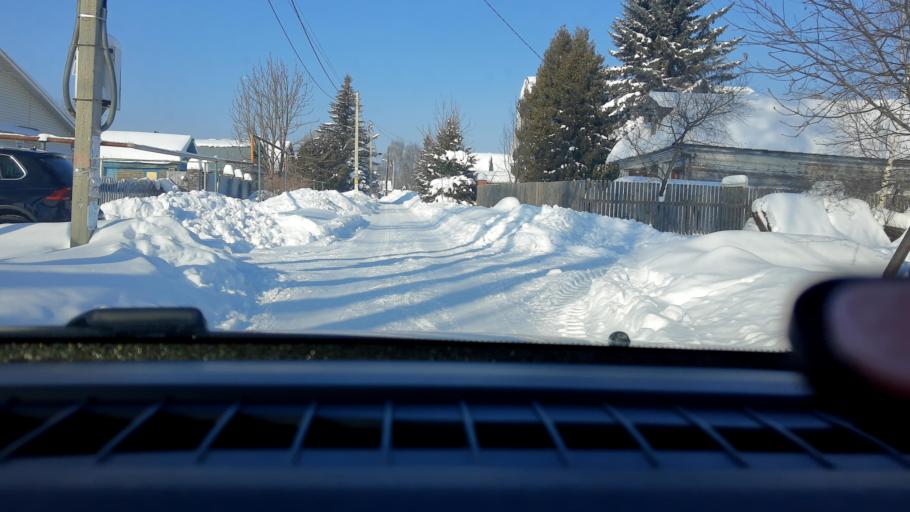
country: RU
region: Nizjnij Novgorod
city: Afonino
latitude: 56.1950
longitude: 44.0540
